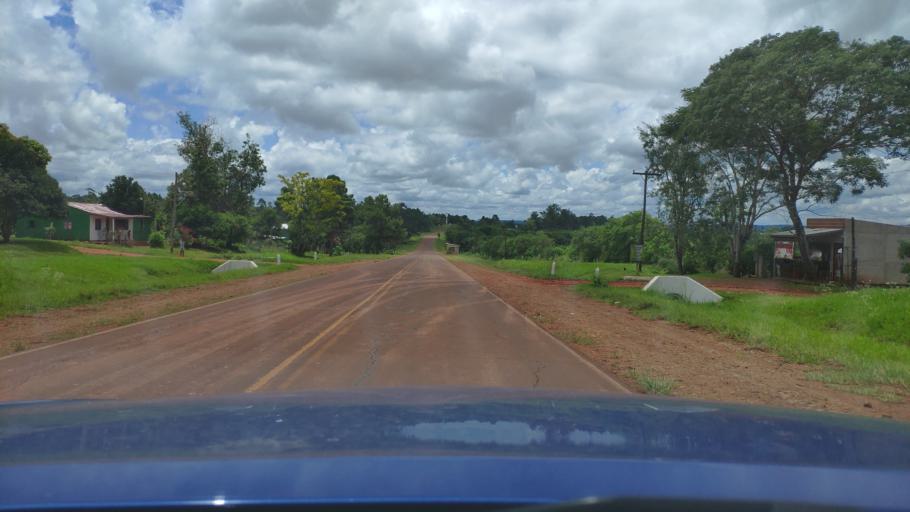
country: AR
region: Misiones
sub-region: Departamento de San Javier
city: San Javier
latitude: -27.8616
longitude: -55.2545
